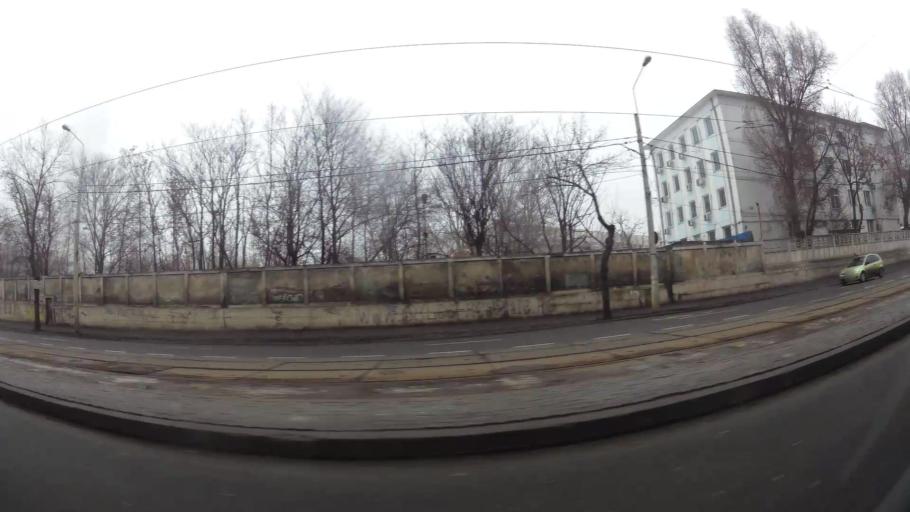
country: RO
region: Bucuresti
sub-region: Municipiul Bucuresti
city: Bucuresti
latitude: 44.4502
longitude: 26.0605
